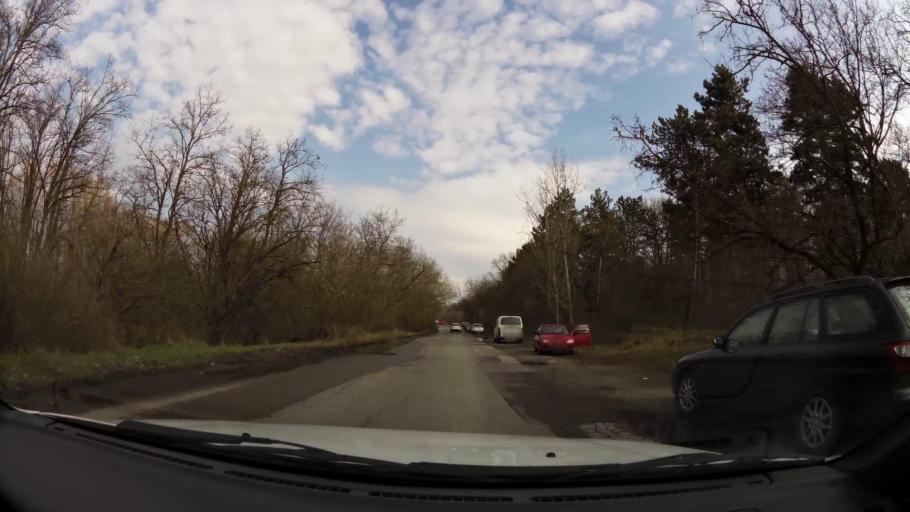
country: HU
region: Budapest
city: Budapest XVII. keruelet
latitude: 47.5088
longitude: 19.2416
